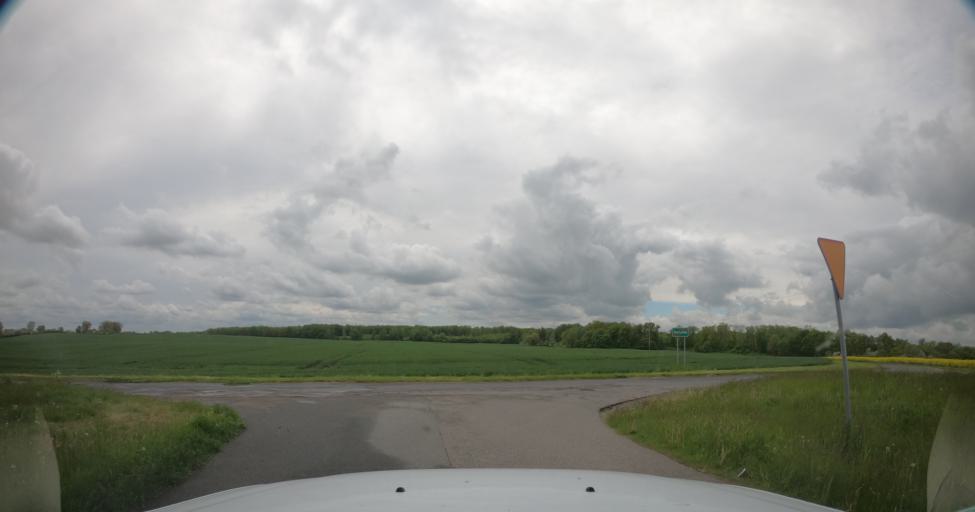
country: PL
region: West Pomeranian Voivodeship
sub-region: Powiat pyrzycki
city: Kozielice
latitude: 53.0822
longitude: 14.8337
